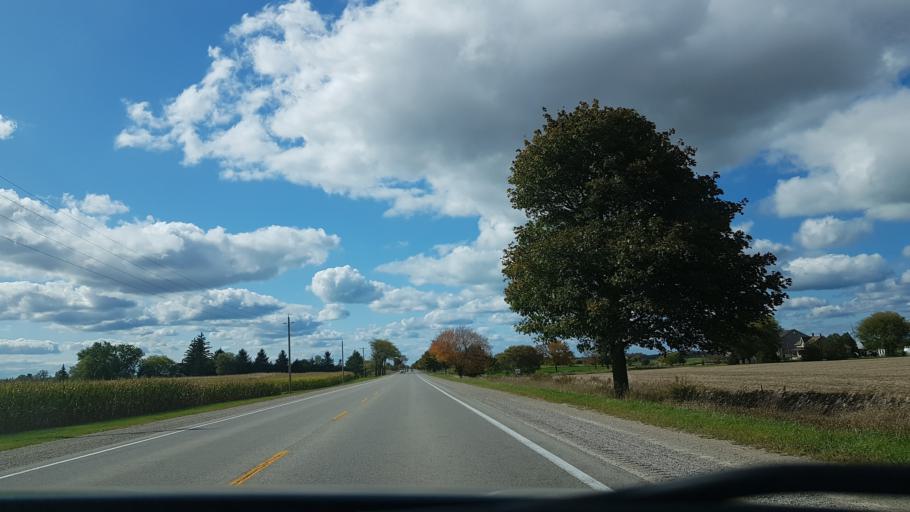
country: CA
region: Ontario
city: Bluewater
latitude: 43.3448
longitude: -81.6478
